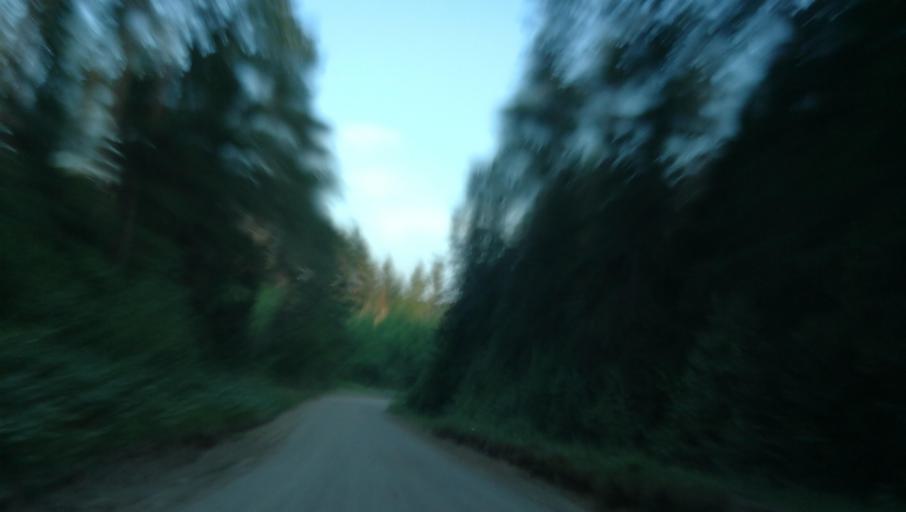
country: LV
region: Cesu Rajons
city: Cesis
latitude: 57.2758
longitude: 25.2231
